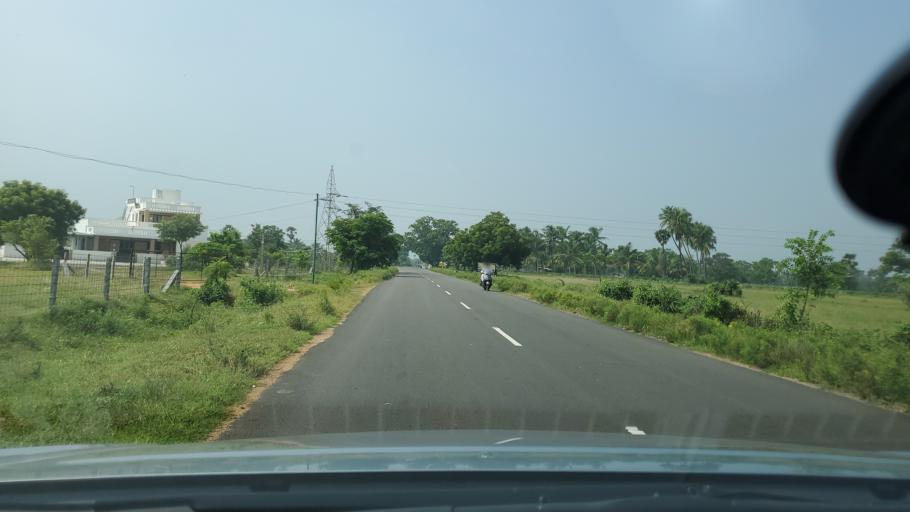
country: IN
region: Tamil Nadu
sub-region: Erode
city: Chennimalai
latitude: 11.1987
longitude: 77.6287
